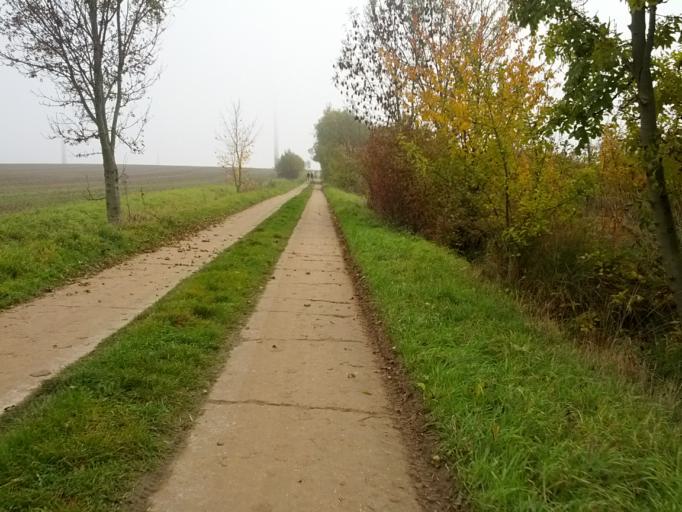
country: DE
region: Thuringia
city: Bischofroda
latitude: 51.0097
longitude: 10.3711
